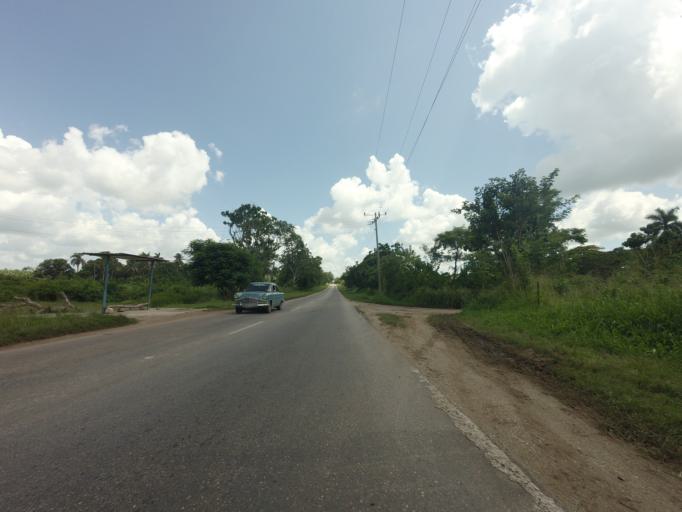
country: CU
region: La Habana
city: Arroyo Naranjo
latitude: 22.9919
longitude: -82.2954
